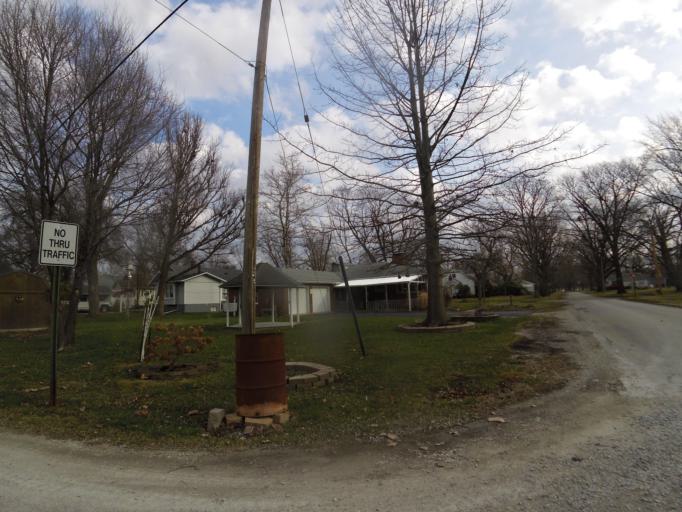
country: US
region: Illinois
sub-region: Christian County
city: Pana
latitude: 39.3779
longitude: -89.0836
